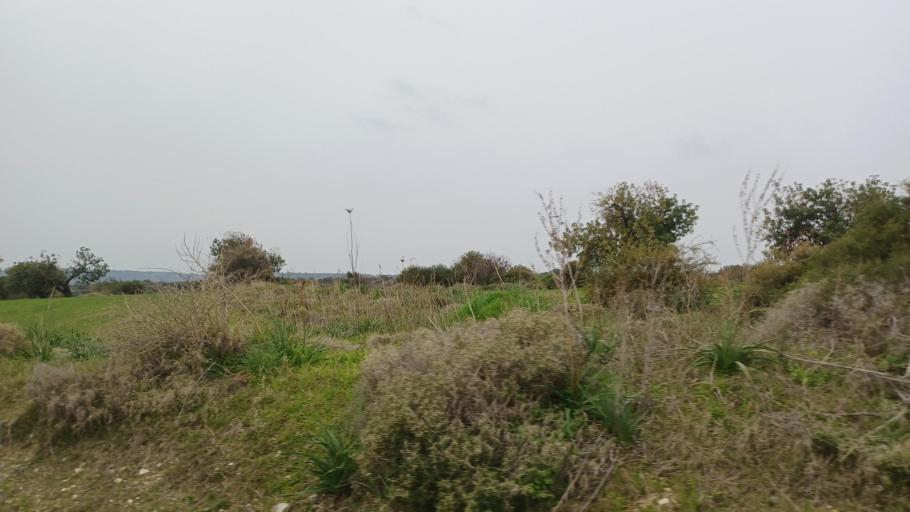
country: CY
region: Limassol
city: Pissouri
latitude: 34.7267
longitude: 32.7375
